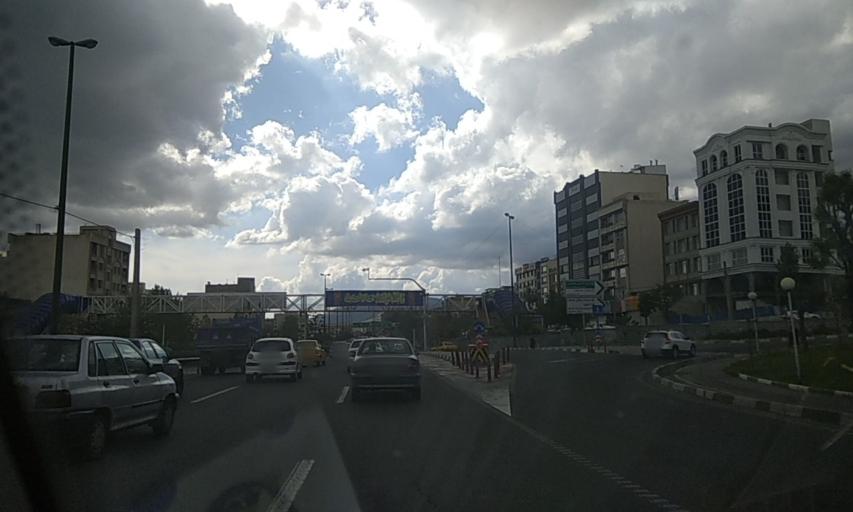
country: IR
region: Tehran
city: Tajrish
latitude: 35.7697
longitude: 51.3283
